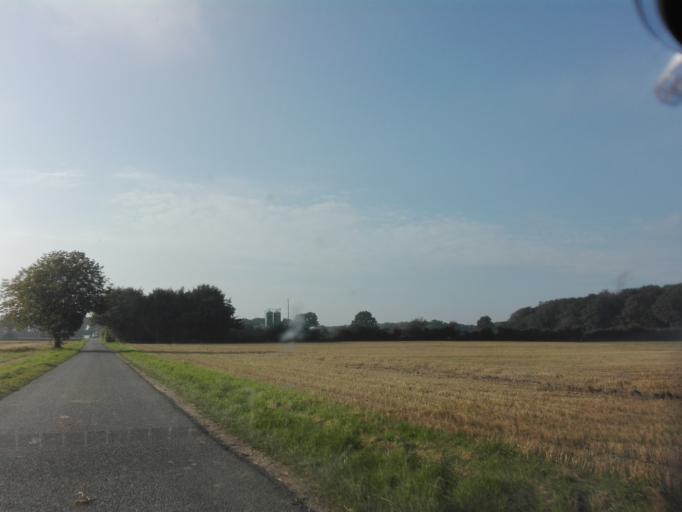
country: DK
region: Central Jutland
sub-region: Odder Kommune
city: Odder
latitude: 55.8717
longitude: 10.1622
